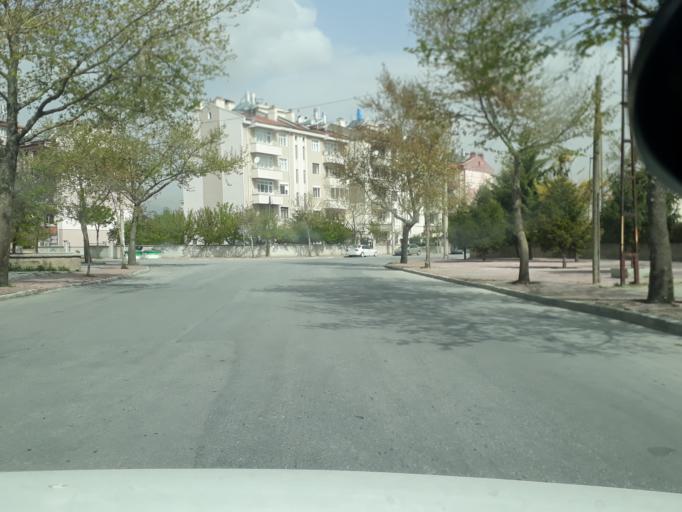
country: TR
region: Konya
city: Selcuklu
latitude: 37.9355
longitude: 32.4995
